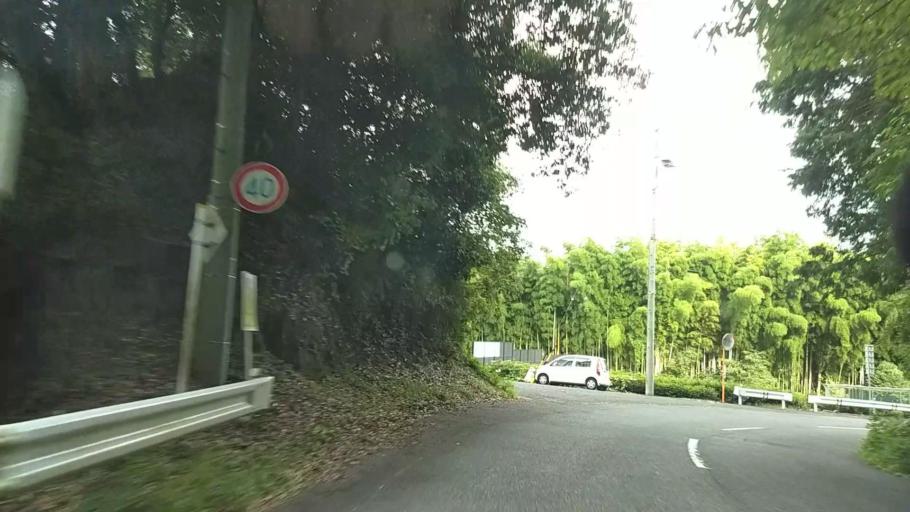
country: JP
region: Shizuoka
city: Fujinomiya
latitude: 35.2055
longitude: 138.5485
